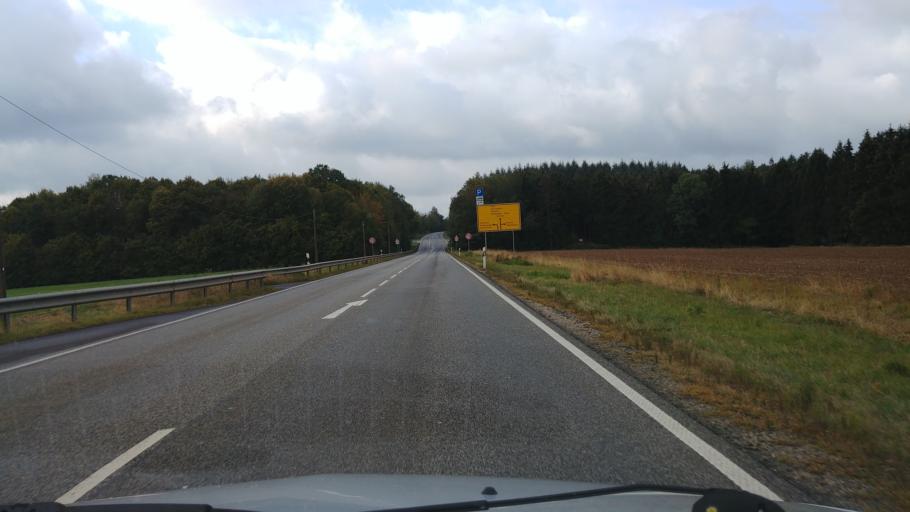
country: DE
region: Rheinland-Pfalz
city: Hochscheid
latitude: 49.8819
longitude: 7.2165
